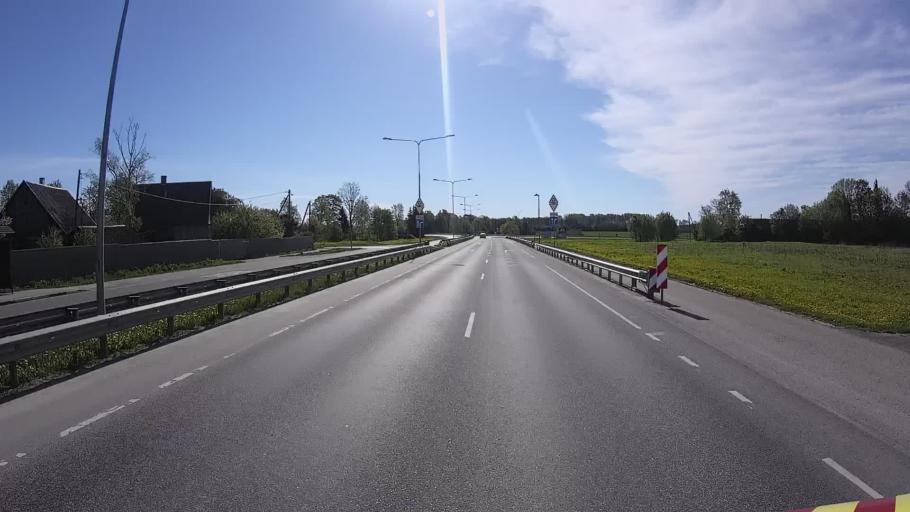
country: EE
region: Tartu
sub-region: Tartu linn
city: Tartu
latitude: 58.3733
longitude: 26.7957
